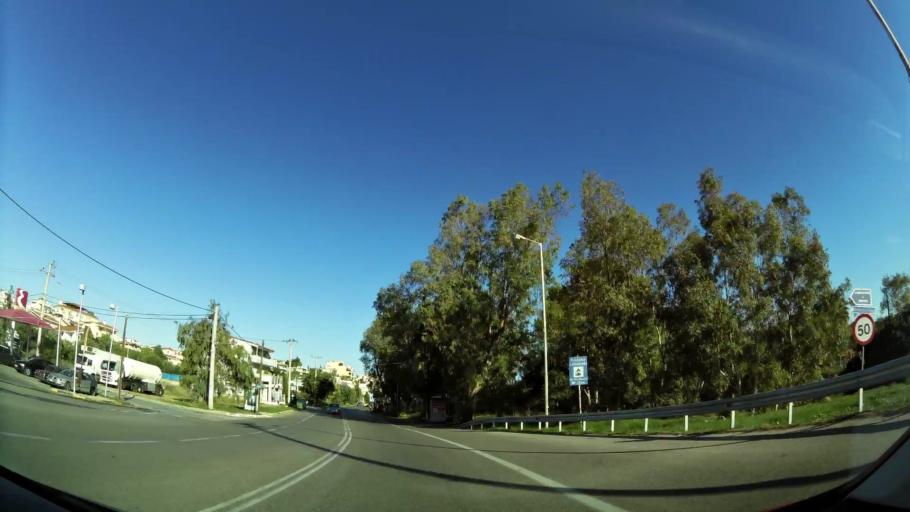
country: GR
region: Attica
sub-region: Nomarchia Anatolikis Attikis
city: Rafina
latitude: 38.0185
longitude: 23.9963
